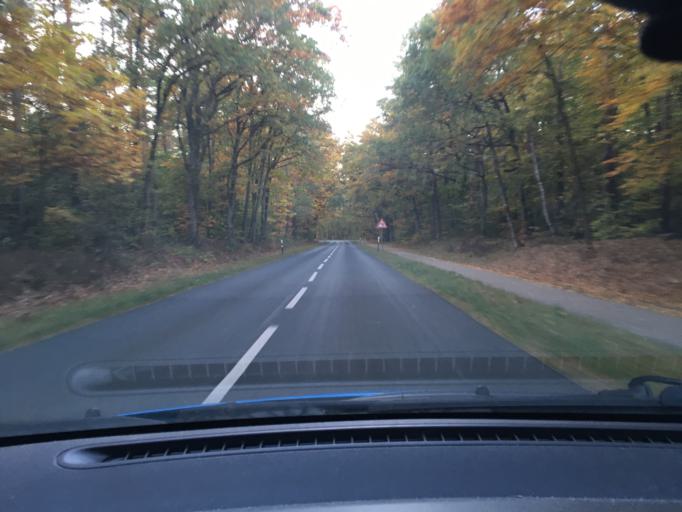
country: DE
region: Lower Saxony
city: Bleckede
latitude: 53.2772
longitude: 10.7739
